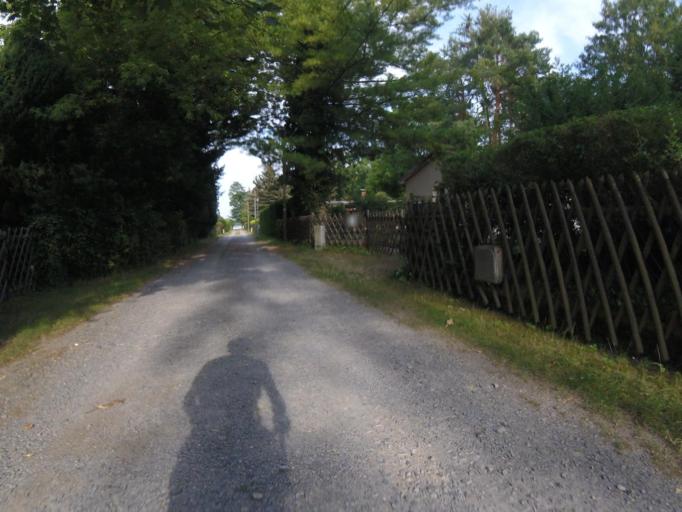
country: DE
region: Brandenburg
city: Munchehofe
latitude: 52.2421
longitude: 13.7757
